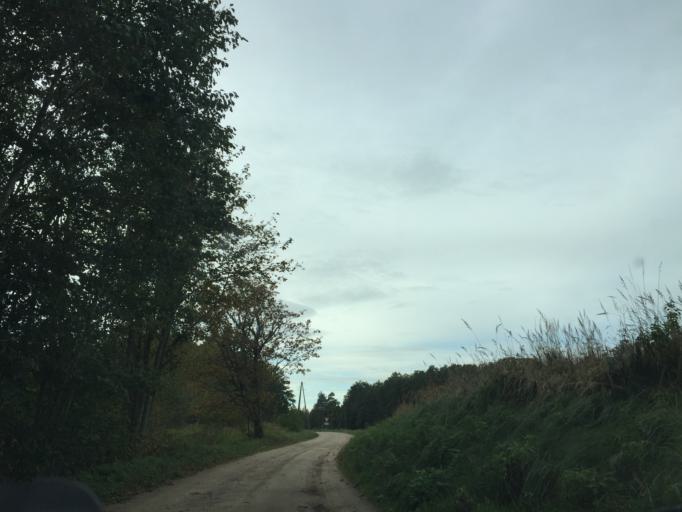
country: LV
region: Auces Novads
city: Auce
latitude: 56.5531
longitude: 23.0216
